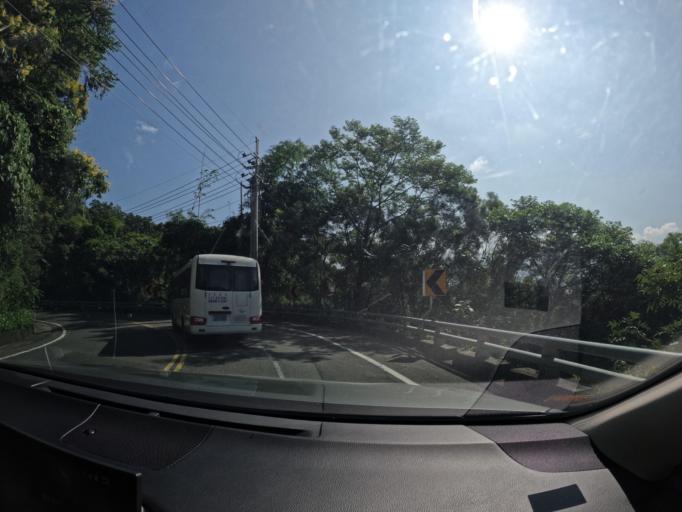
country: TW
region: Taiwan
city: Yujing
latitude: 23.0702
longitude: 120.6389
